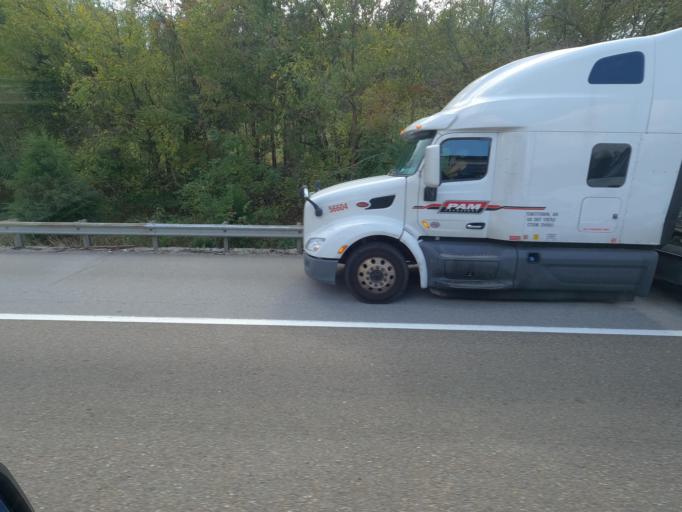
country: US
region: Tennessee
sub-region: Loudon County
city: Lenoir City
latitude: 35.8713
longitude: -84.2666
